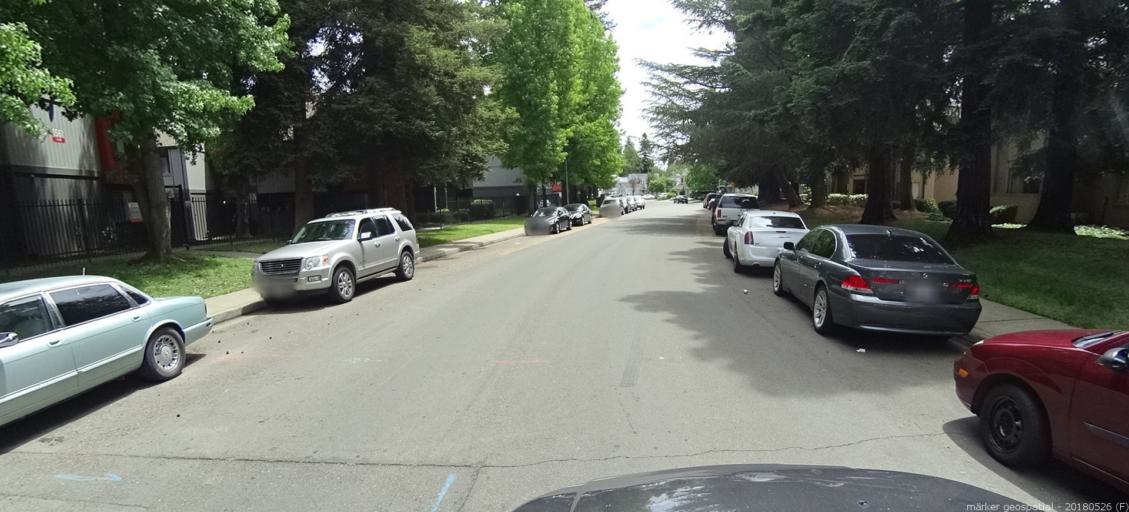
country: US
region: California
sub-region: Sacramento County
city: Sacramento
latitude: 38.6110
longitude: -121.4954
